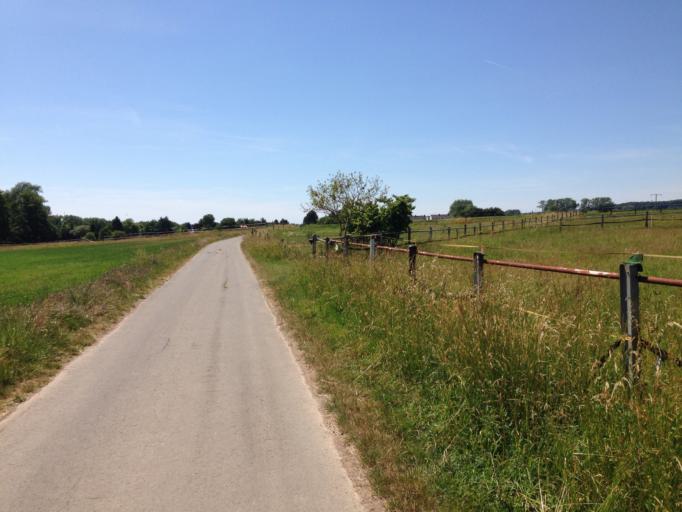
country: DE
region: Hesse
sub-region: Regierungsbezirk Giessen
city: Alten Buseck
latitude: 50.6123
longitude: 8.7675
